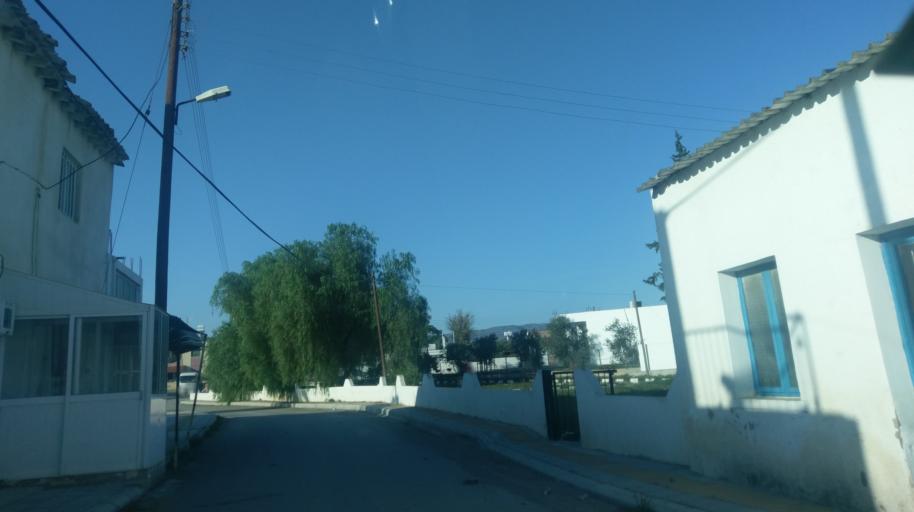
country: CY
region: Ammochostos
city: Lefkonoiko
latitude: 35.2638
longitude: 33.6624
